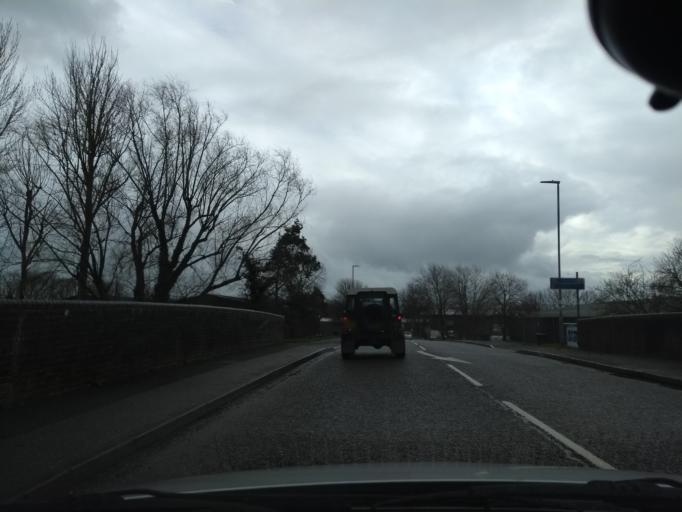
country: GB
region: England
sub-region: Somerset
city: Taunton
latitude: 51.0297
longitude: -3.0804
